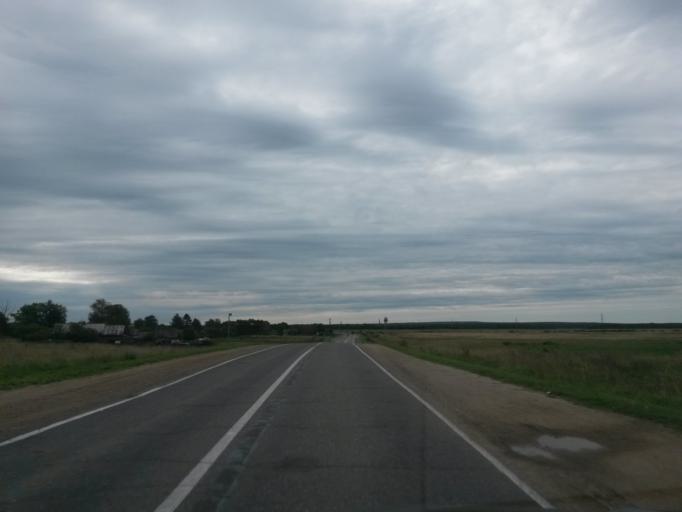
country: RU
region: Jaroslavl
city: Gavrilov-Yam
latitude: 57.3347
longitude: 39.8103
